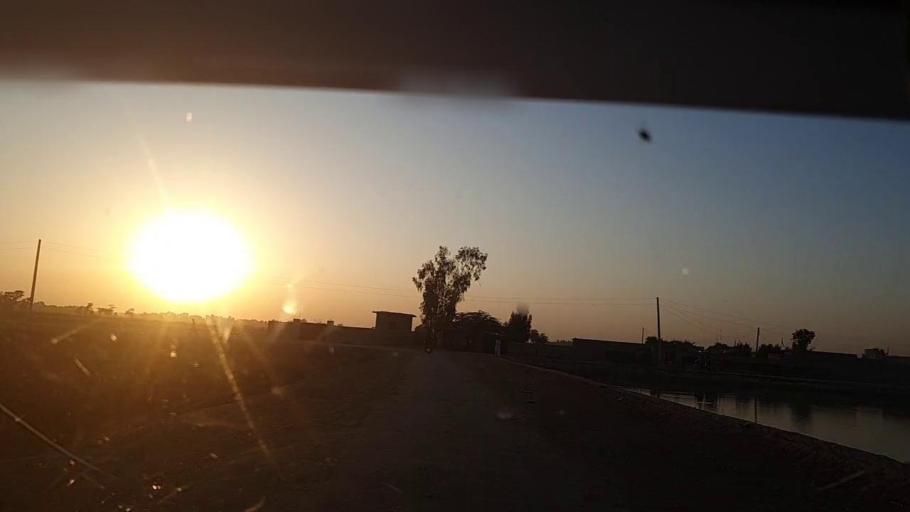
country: PK
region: Sindh
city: Ratodero
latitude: 27.8914
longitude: 68.2371
